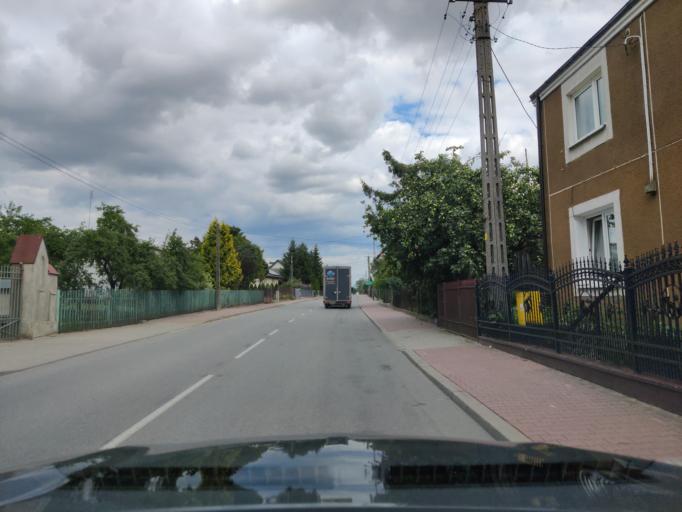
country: PL
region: Masovian Voivodeship
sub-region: Powiat sokolowski
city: Kosow Lacki
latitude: 52.5960
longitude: 22.1482
